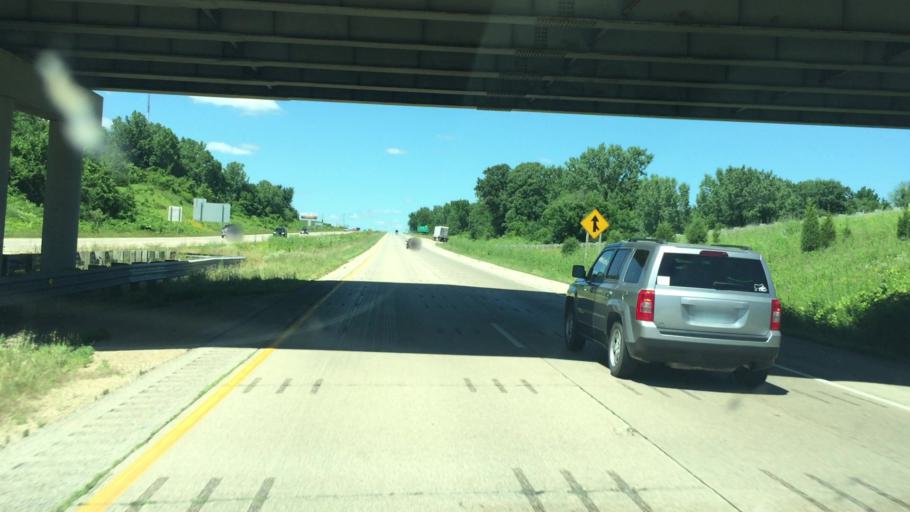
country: US
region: Illinois
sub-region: Jo Daviess County
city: East Dubuque
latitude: 42.5206
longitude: -90.6146
